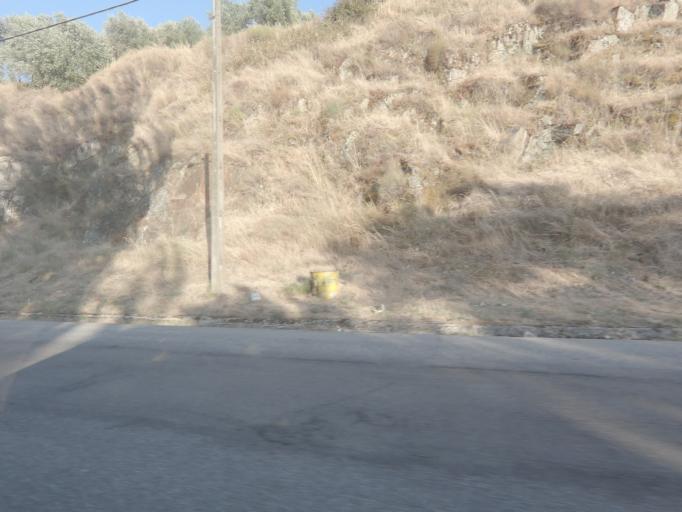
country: PT
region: Viseu
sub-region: Armamar
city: Armamar
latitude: 41.1552
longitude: -7.6750
